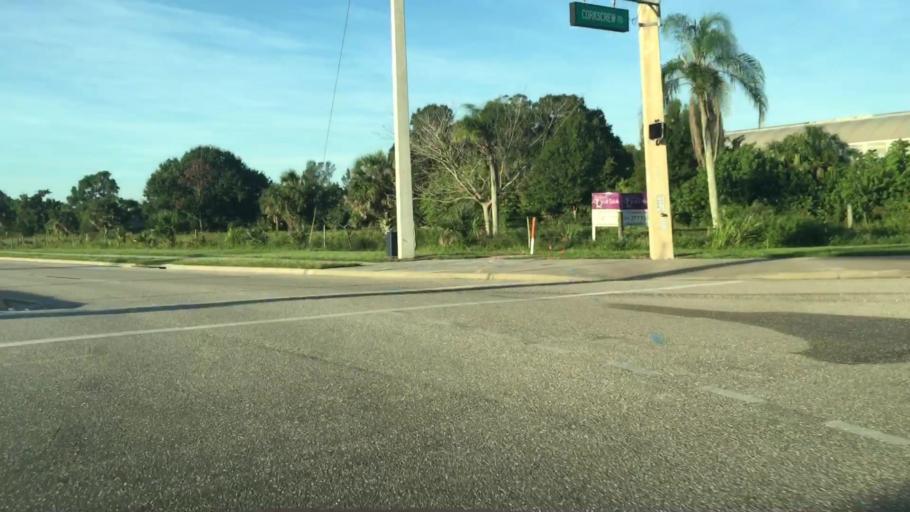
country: US
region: Florida
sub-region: Lee County
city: Estero
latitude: 26.4311
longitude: -81.8050
